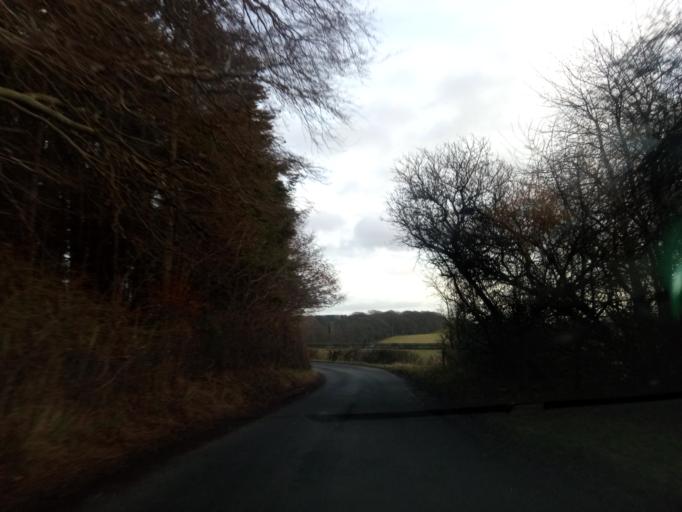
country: GB
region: Scotland
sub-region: The Scottish Borders
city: Newtown St Boswells
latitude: 55.5515
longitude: -2.6917
